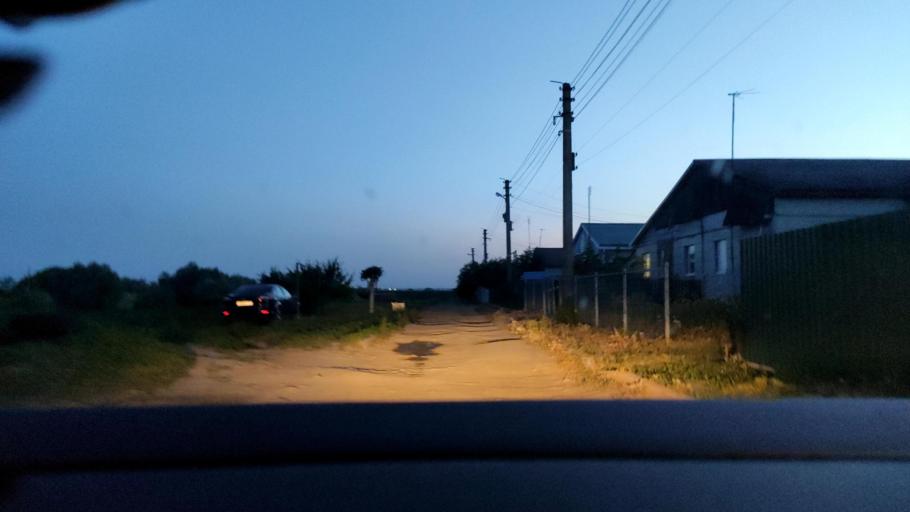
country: RU
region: Voronezj
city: Maslovka
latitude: 51.5010
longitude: 39.3005
